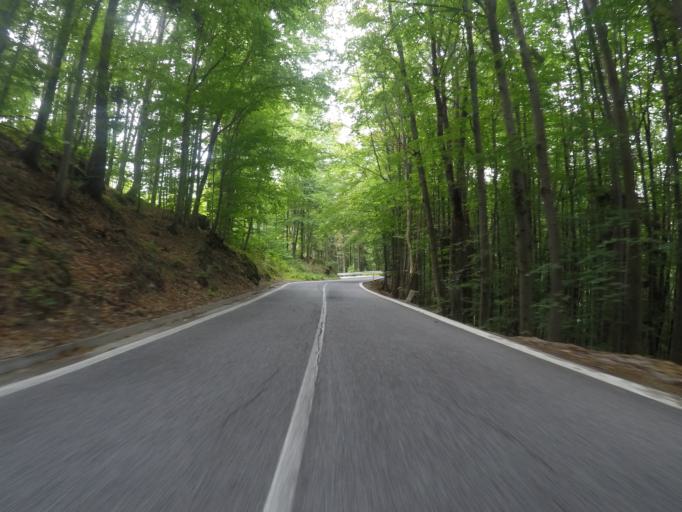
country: SK
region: Kosicky
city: Dobsina
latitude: 48.8507
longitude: 20.4600
